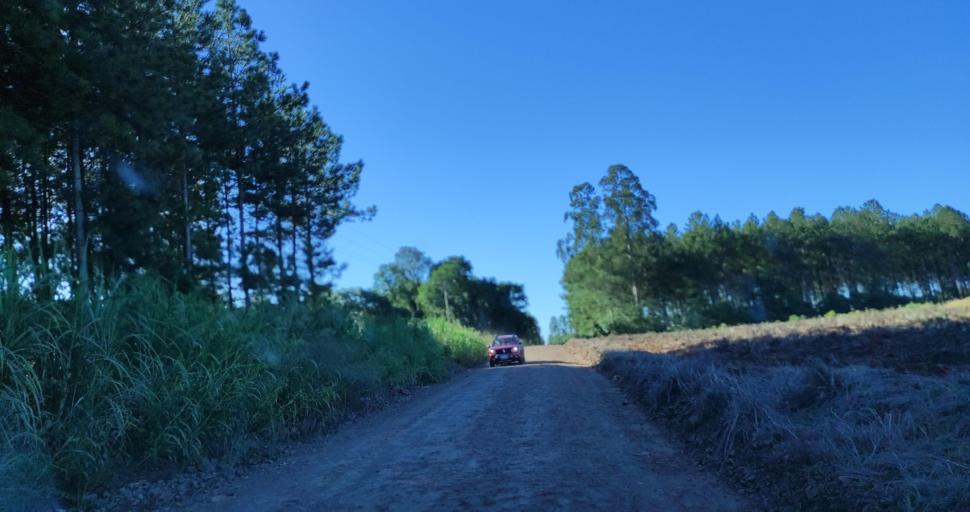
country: AR
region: Misiones
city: Capiovi
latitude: -26.8860
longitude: -54.9968
